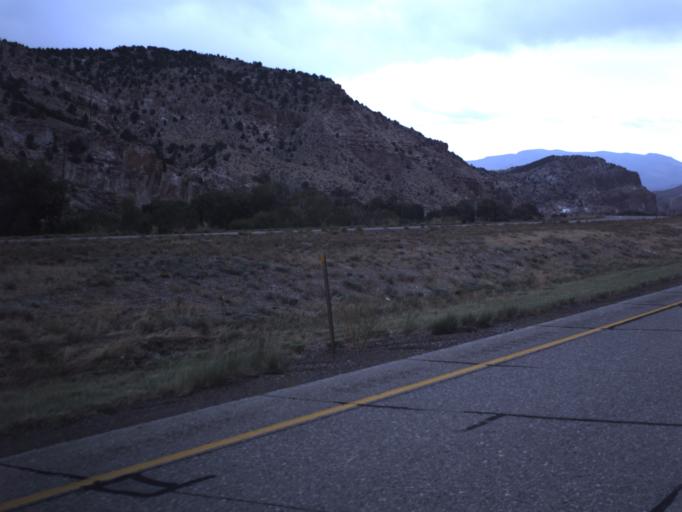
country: US
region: Utah
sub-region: Sevier County
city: Monroe
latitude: 38.5775
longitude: -112.3218
